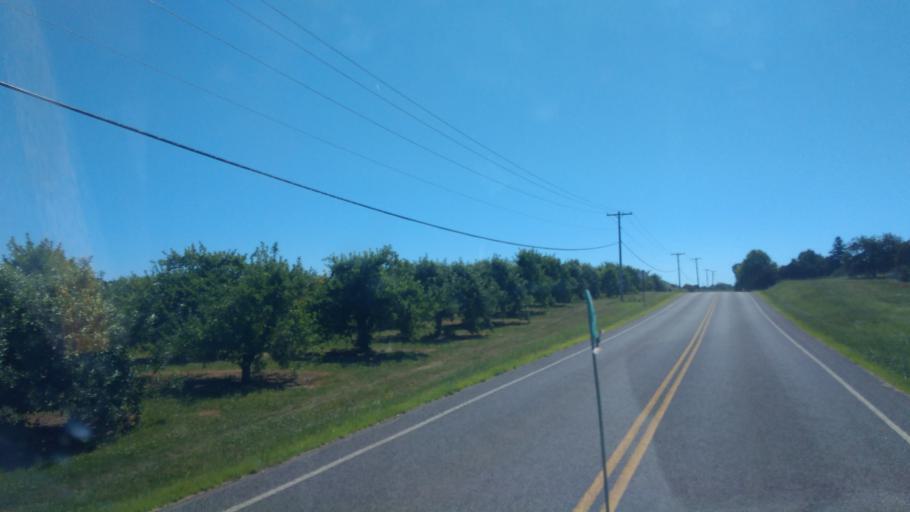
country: US
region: New York
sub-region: Wayne County
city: Sodus
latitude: 43.2749
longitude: -77.1122
